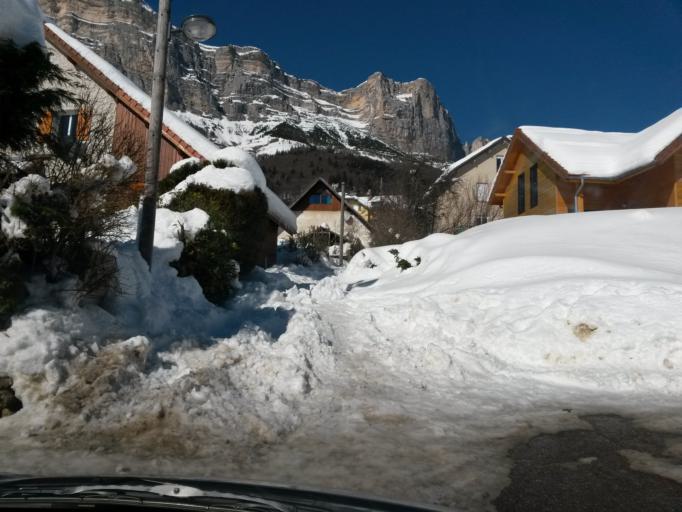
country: FR
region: Rhone-Alpes
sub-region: Departement de l'Isere
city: Saint-Hilaire
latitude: 45.3004
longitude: 5.8740
